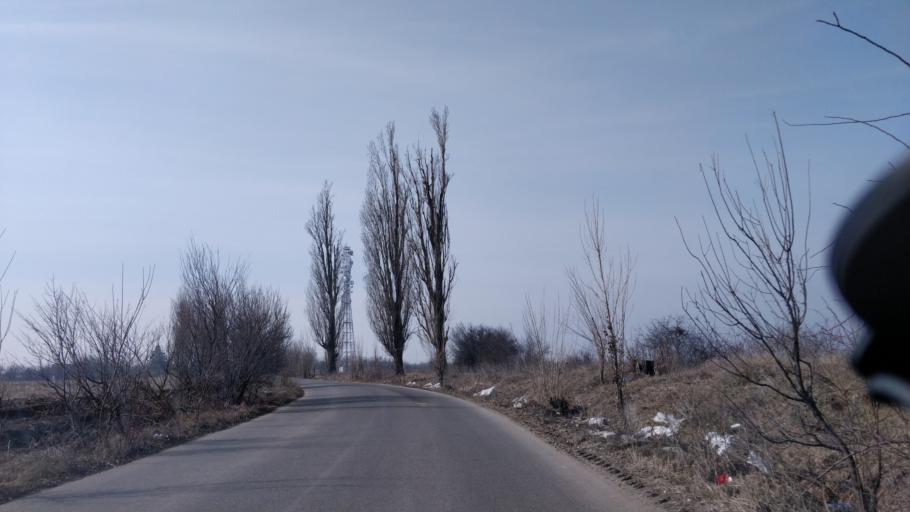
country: RO
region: Giurgiu
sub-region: Comuna Ulmi
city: Ulmi
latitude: 44.4641
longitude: 25.7930
